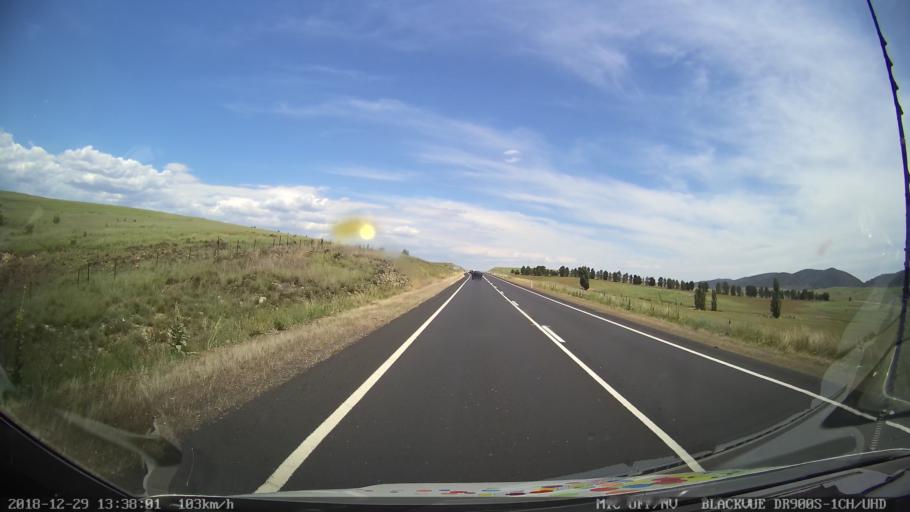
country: AU
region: New South Wales
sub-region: Cooma-Monaro
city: Cooma
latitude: -35.9925
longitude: 149.1393
